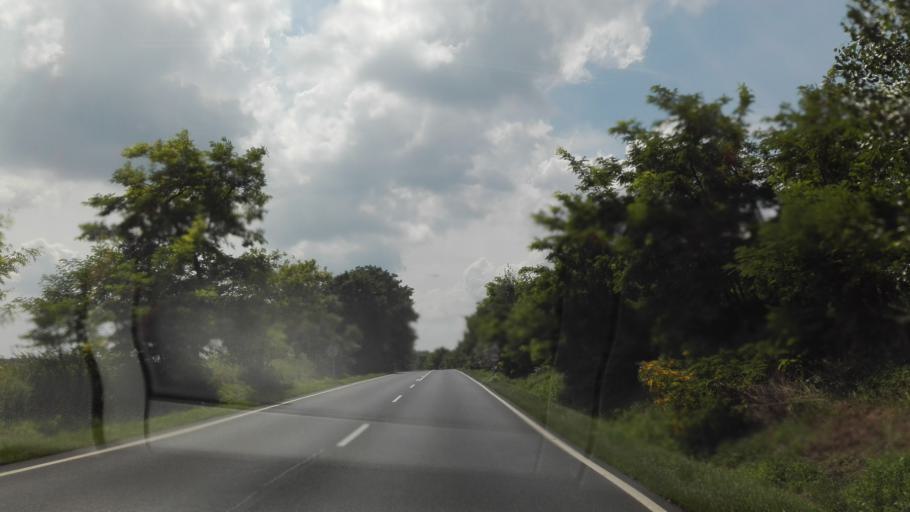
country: HU
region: Fejer
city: Eloszallas
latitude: 46.8123
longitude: 18.7813
